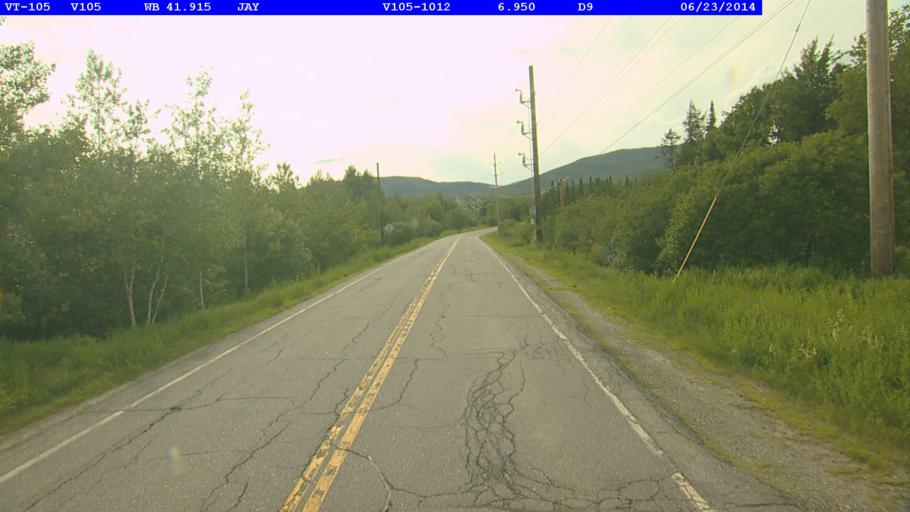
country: CA
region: Quebec
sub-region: Monteregie
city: Sutton
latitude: 44.9702
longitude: -72.4494
